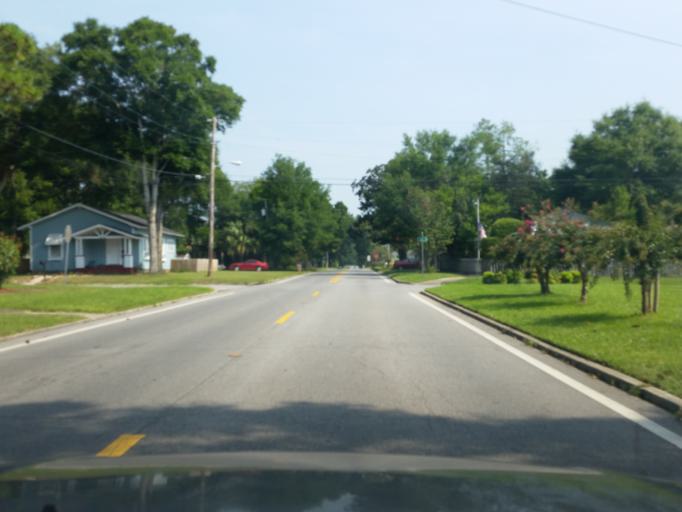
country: US
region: Florida
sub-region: Escambia County
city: East Pensacola Heights
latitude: 30.4304
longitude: -87.1965
